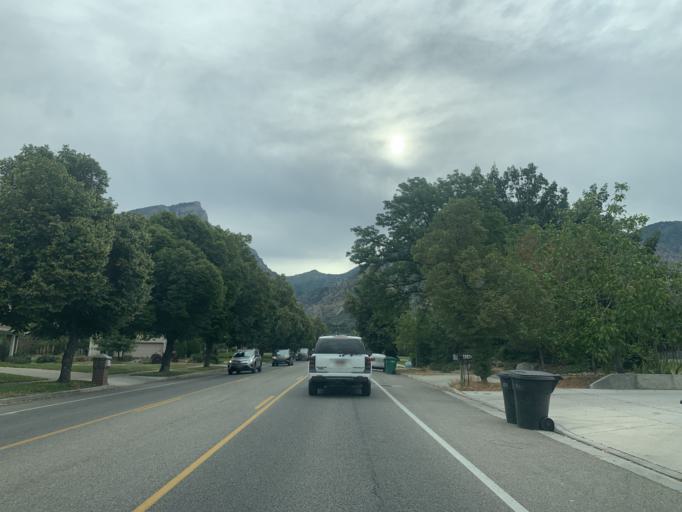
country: US
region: Utah
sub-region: Utah County
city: Provo
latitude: 40.2630
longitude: -111.6510
